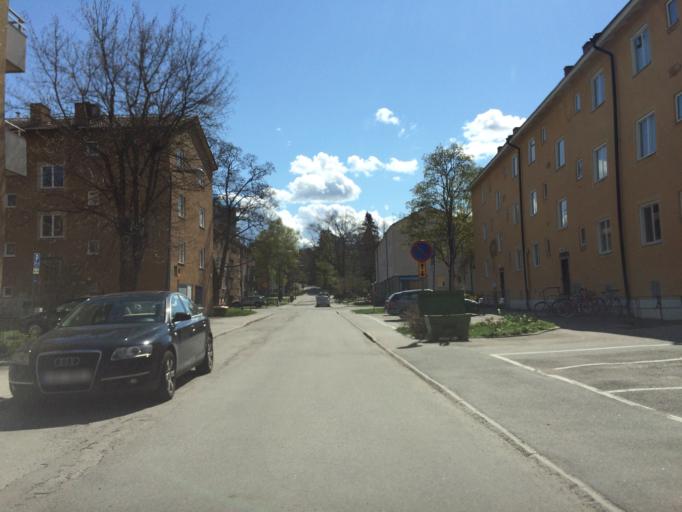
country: SE
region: Stockholm
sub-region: Huddinge Kommun
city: Segeltorp
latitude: 59.2965
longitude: 17.9718
